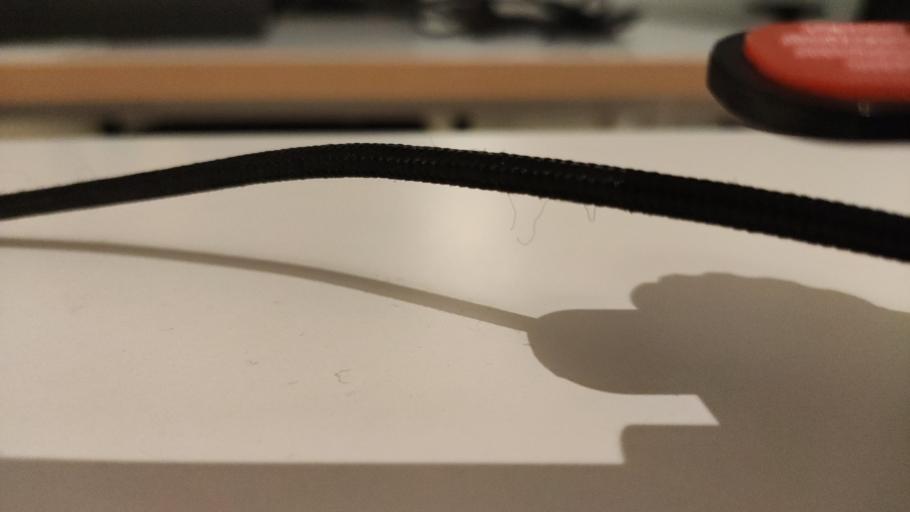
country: RU
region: Moskovskaya
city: Novoye
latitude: 55.6339
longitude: 38.9307
